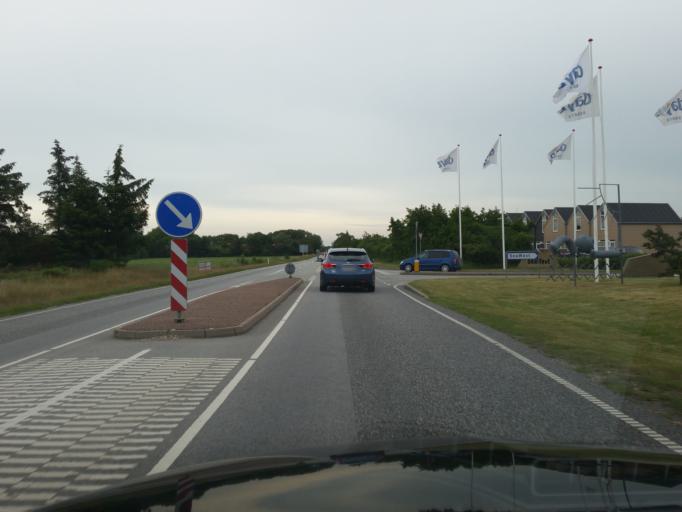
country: DK
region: South Denmark
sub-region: Varde Kommune
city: Oksbol
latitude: 55.7883
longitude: 8.2494
